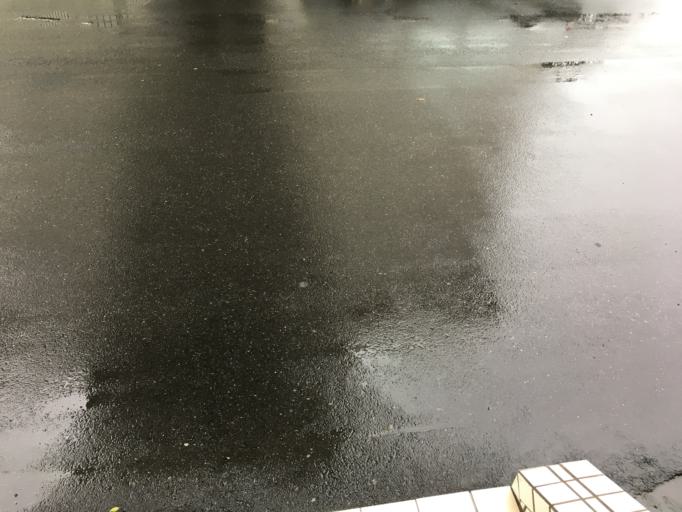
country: TW
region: Taiwan
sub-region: Yilan
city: Yilan
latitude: 24.7220
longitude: 121.6876
